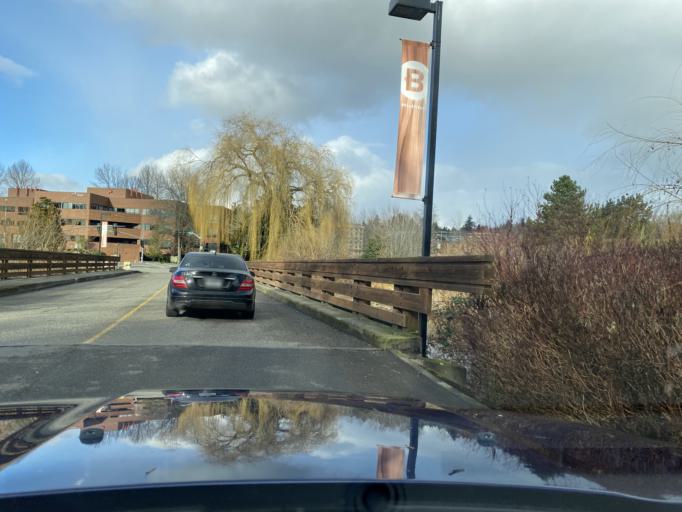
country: US
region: Washington
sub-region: King County
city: Bellevue
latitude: 47.6006
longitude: -122.1877
